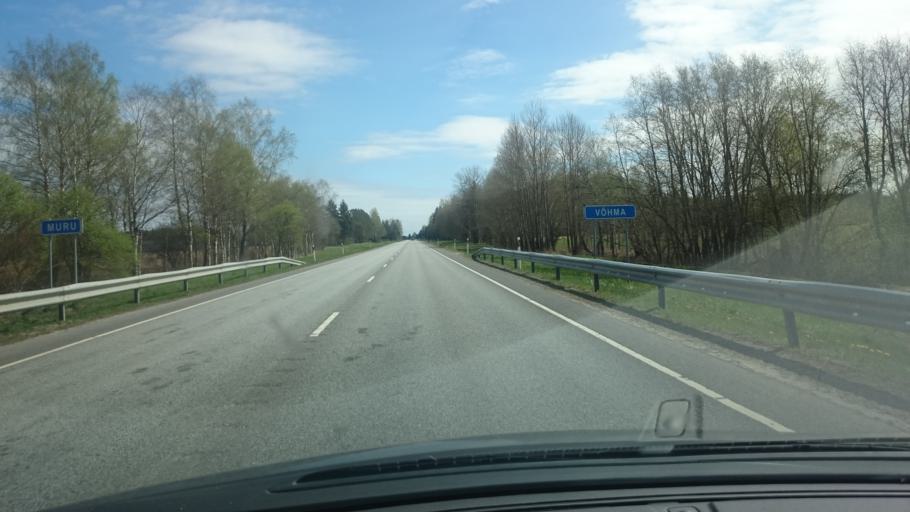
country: EE
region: Laeaene-Virumaa
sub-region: Someru vald
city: Someru
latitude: 59.3683
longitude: 26.5353
